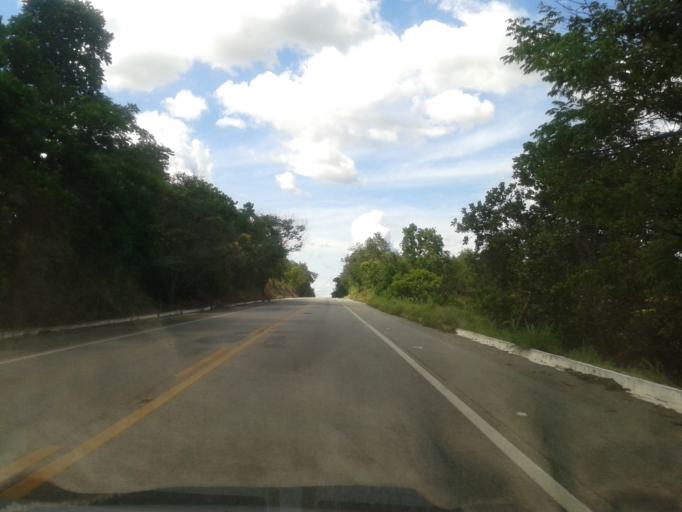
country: BR
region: Goias
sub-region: Itapuranga
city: Itapuranga
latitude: -15.5402
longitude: -50.2901
